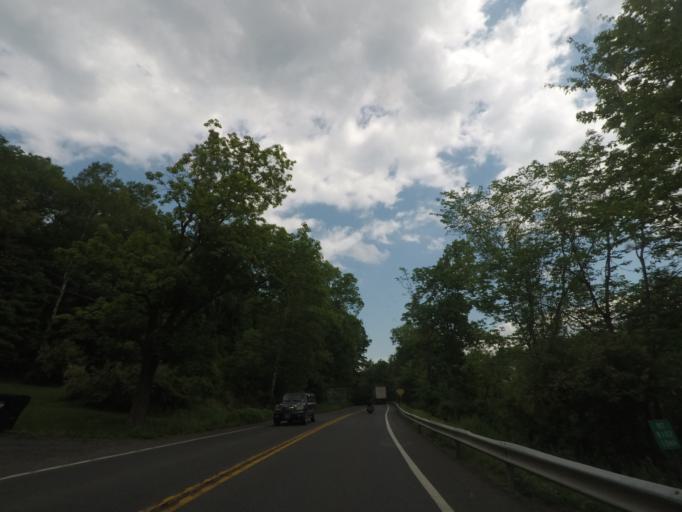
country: US
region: New York
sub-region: Dutchess County
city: Pine Plains
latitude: 42.0533
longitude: -73.6439
